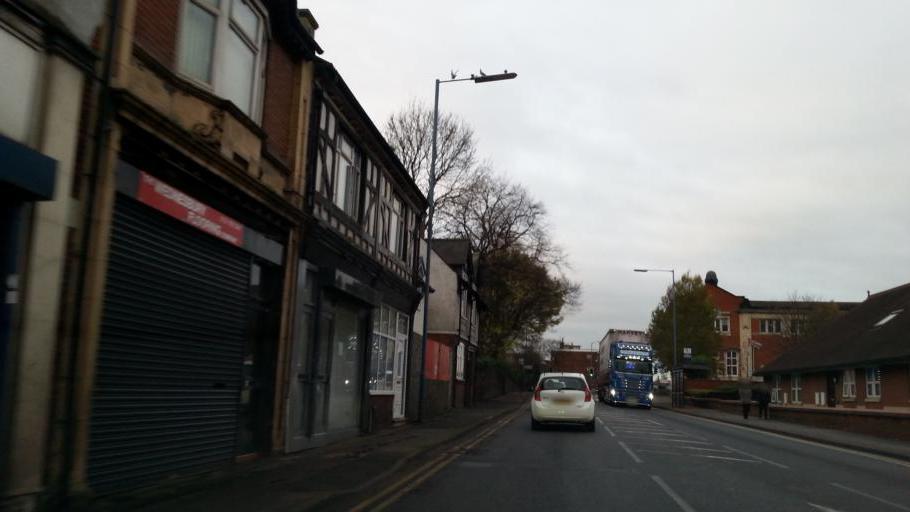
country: GB
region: England
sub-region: Sandwell
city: Wednesbury
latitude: 52.5539
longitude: -2.0152
